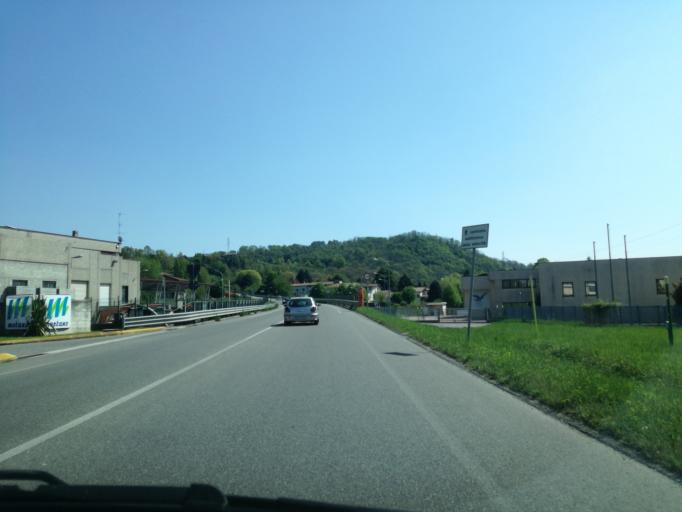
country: IT
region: Lombardy
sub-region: Provincia di Bergamo
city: Villa d'Adda
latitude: 45.7114
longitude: 9.4581
